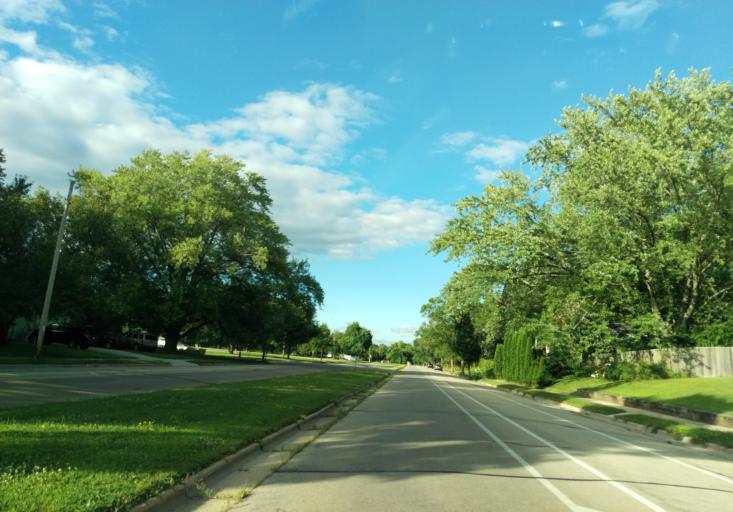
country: US
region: Wisconsin
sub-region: Dane County
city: Shorewood Hills
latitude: 43.0549
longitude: -89.4634
